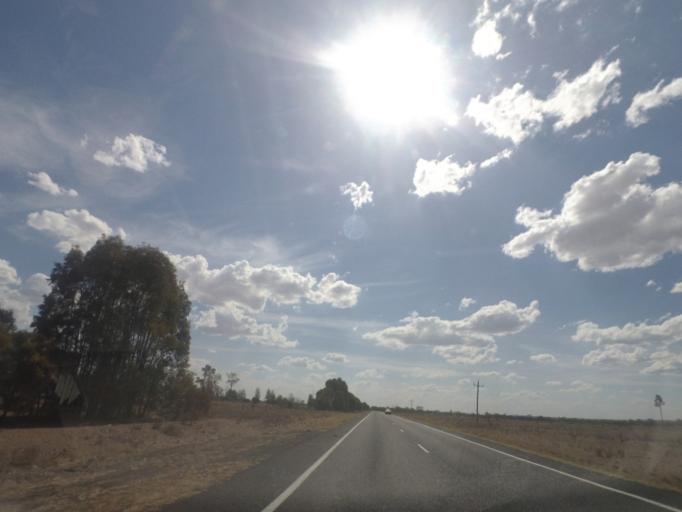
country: AU
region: New South Wales
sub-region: Moree Plains
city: Boggabilla
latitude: -28.4147
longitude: 151.1325
